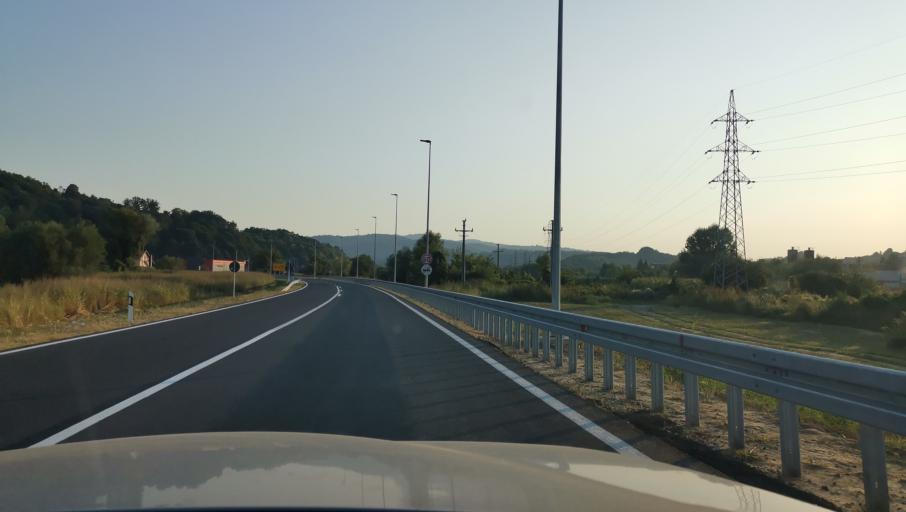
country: RS
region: Central Serbia
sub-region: Kolubarski Okrug
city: Ljig
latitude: 44.2312
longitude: 20.2483
